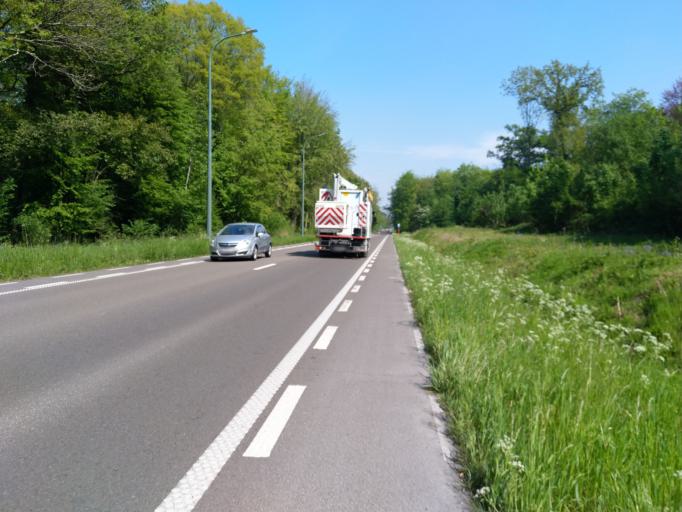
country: BE
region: Wallonia
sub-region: Province du Hainaut
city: Mons
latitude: 50.4619
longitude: 4.0194
